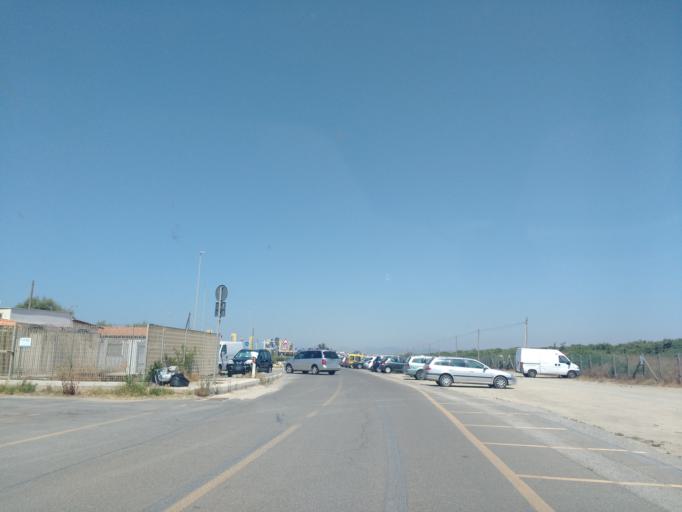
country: IT
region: Latium
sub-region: Citta metropolitana di Roma Capitale
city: Passo Oscuro
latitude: 41.8771
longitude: 12.1771
